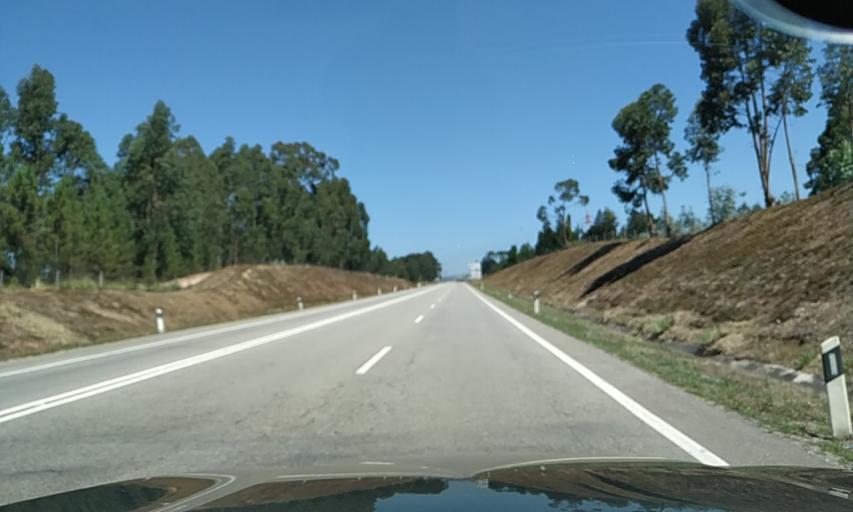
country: PT
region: Aveiro
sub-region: Agueda
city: Agueda
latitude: 40.5846
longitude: -8.4720
